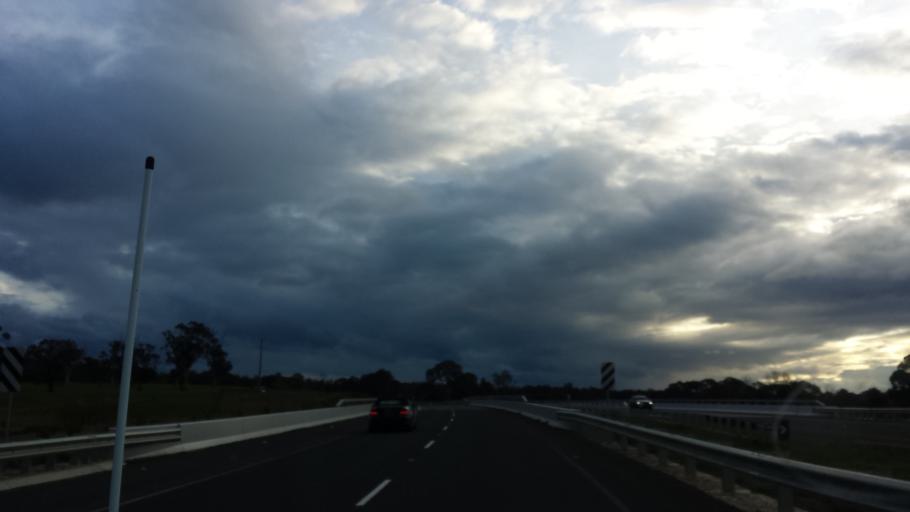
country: AU
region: Victoria
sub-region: Latrobe
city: Traralgon
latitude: -38.1585
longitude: 146.7113
